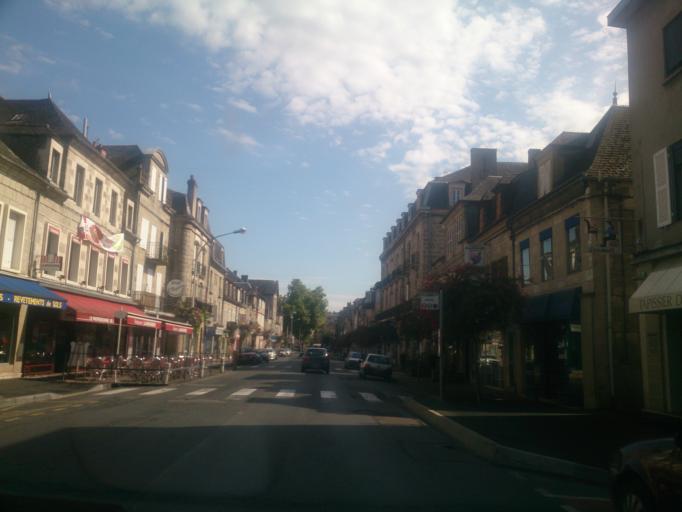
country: FR
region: Limousin
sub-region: Departement de la Correze
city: Brive-la-Gaillarde
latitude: 45.1642
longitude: 1.5322
